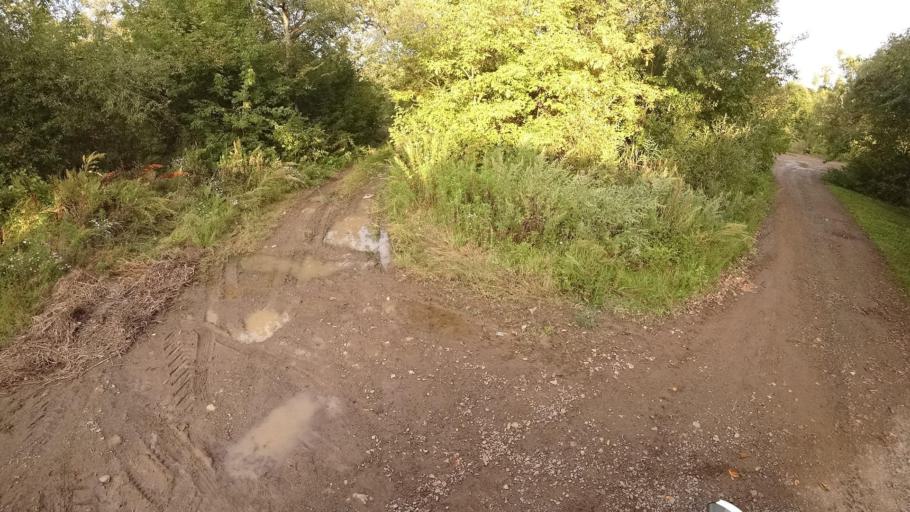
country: RU
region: Primorskiy
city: Yakovlevka
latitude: 44.4228
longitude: 133.4895
